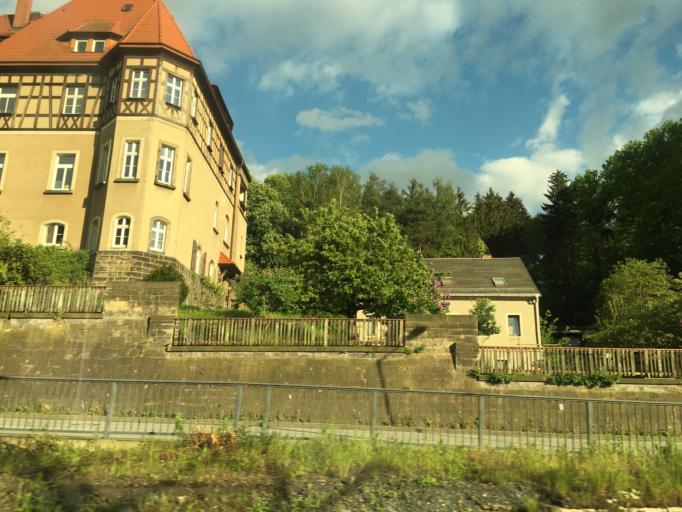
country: DE
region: Saxony
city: Konigstein
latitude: 50.9219
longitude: 14.0886
